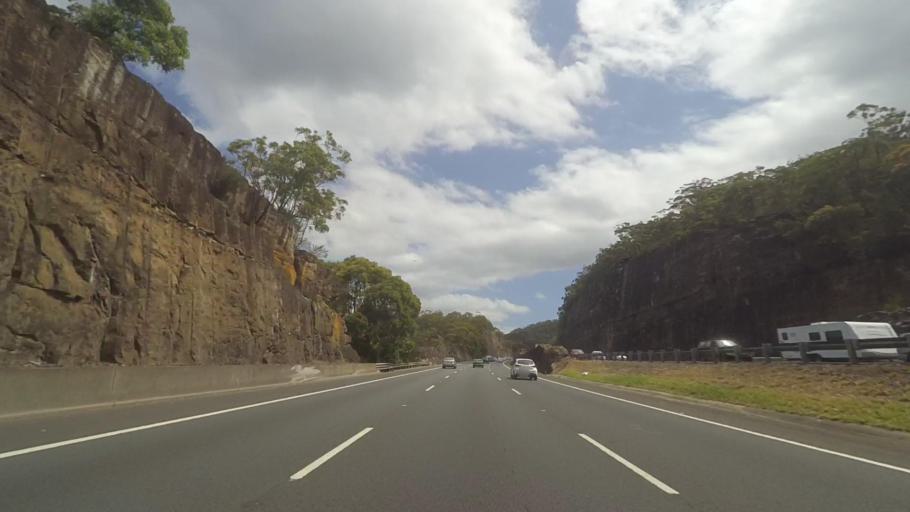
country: AU
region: New South Wales
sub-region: Hornsby Shire
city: Berowra
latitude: -33.5458
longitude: 151.1969
